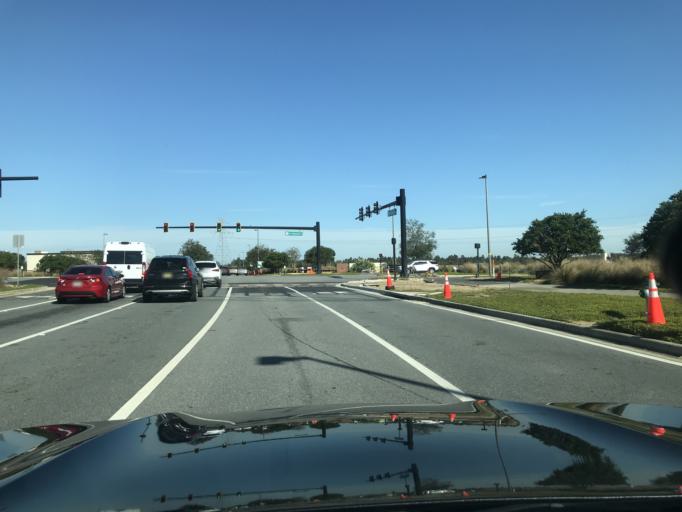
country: US
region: Florida
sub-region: Orange County
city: Oakland
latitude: 28.4739
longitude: -81.6264
